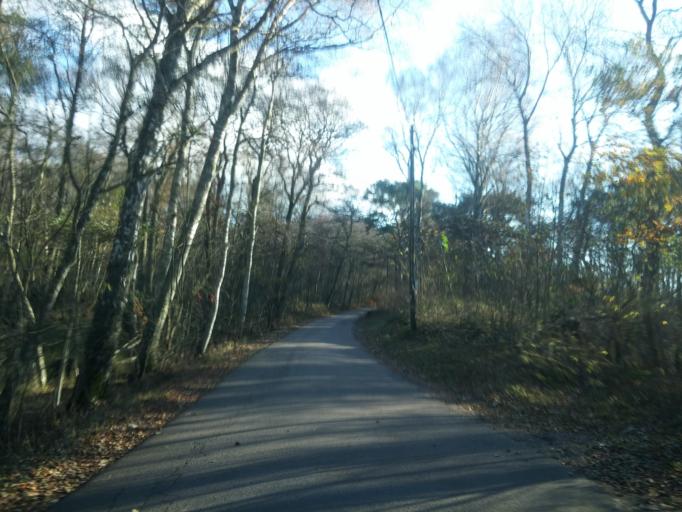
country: SE
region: Skane
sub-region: Angelholms Kommun
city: AEngelholm
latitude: 56.2347
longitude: 12.8195
